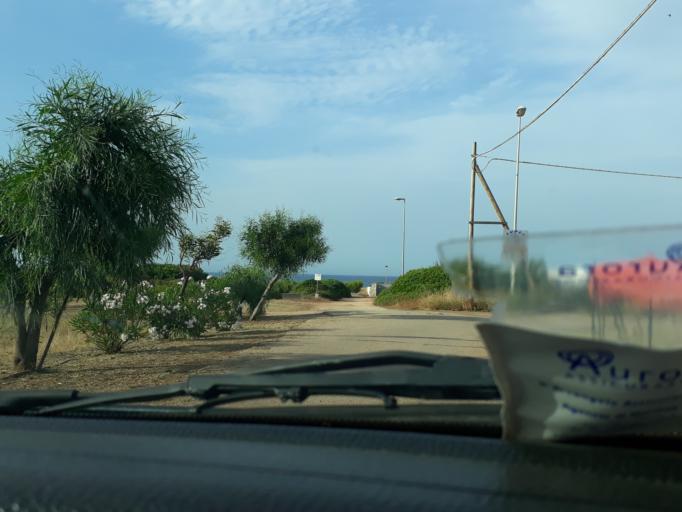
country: IT
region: Apulia
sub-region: Provincia di Brindisi
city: Carovigno
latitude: 40.7633
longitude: 17.6859
